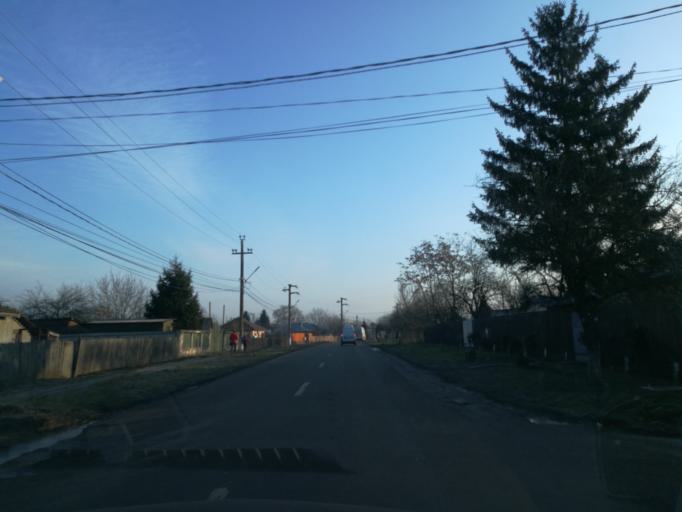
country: RO
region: Ilfov
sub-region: Comuna Moara Vlasiei
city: Moara Vlasiei
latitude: 44.6407
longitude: 26.2007
